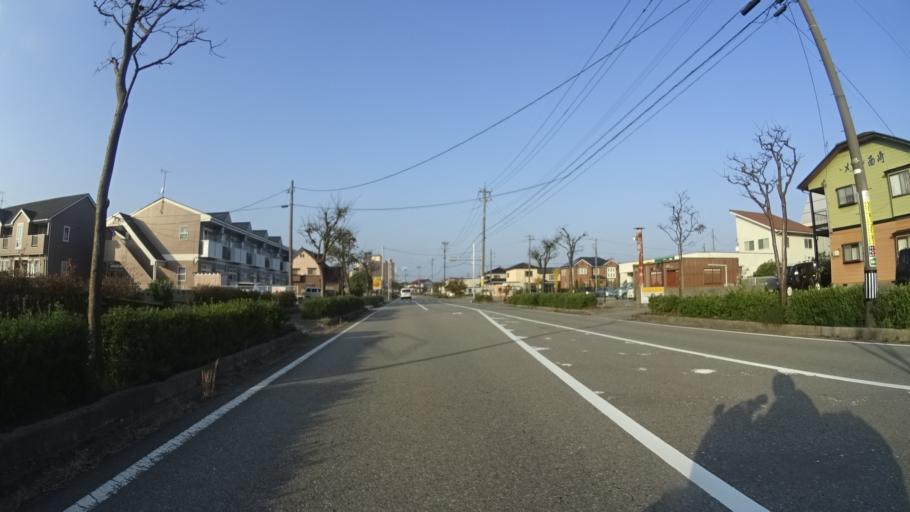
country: JP
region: Ishikawa
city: Nanao
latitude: 37.0799
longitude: 136.9262
